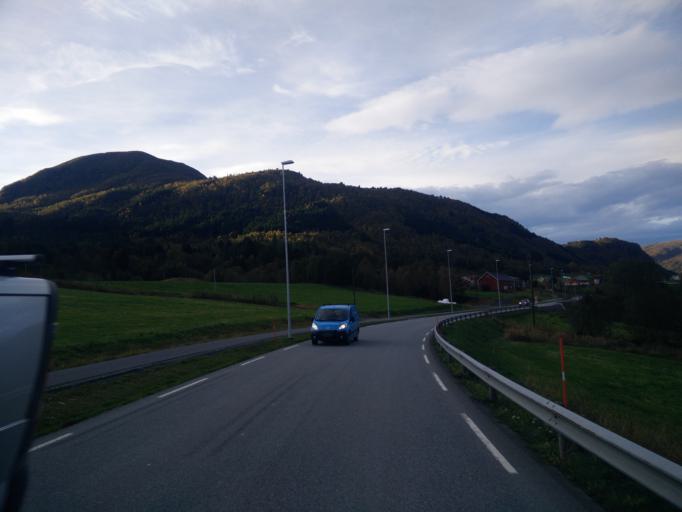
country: NO
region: More og Romsdal
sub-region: Gjemnes
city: Batnfjordsora
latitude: 62.8769
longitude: 7.6476
